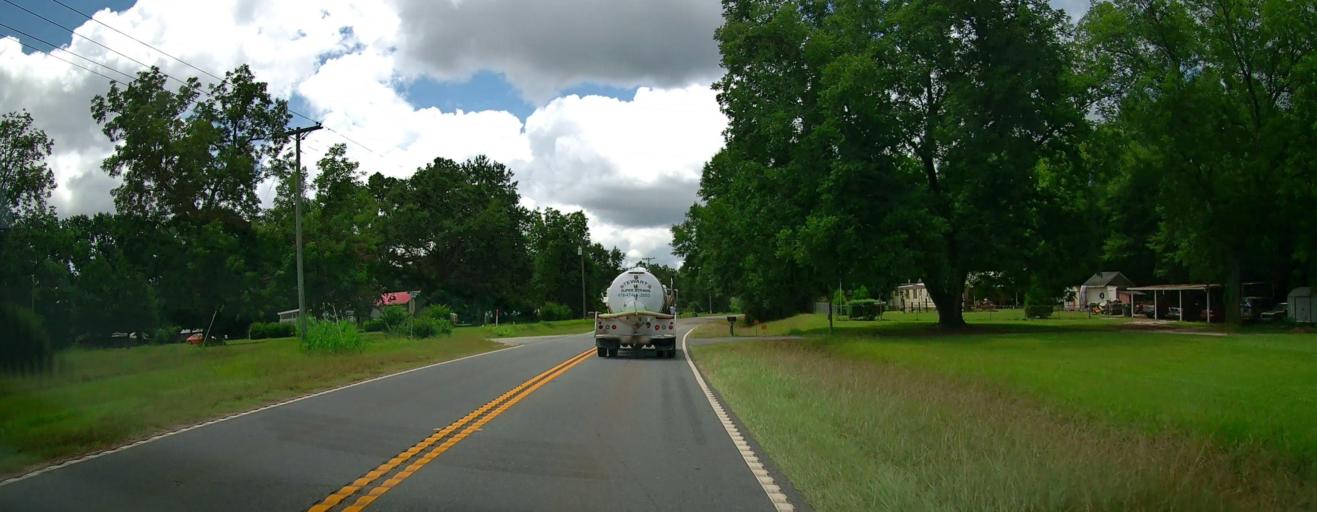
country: US
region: Georgia
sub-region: Houston County
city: Perry
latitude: 32.4575
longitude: -83.6186
